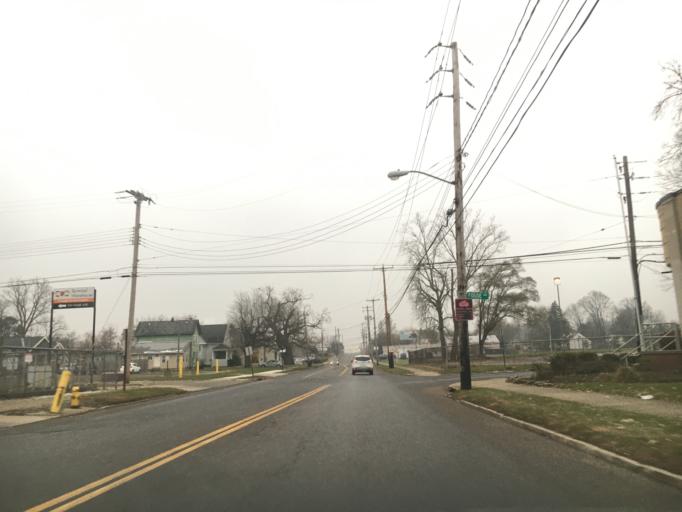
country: US
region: Ohio
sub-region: Summit County
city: Akron
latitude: 41.0982
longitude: -81.4884
